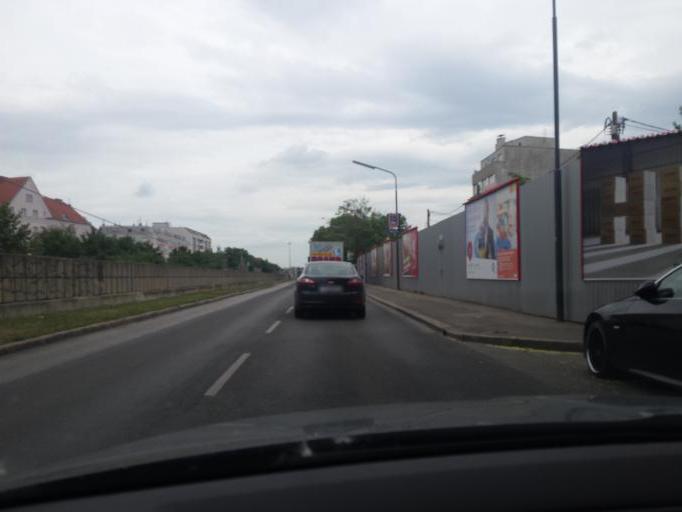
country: AT
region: Vienna
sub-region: Wien Stadt
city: Vienna
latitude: 48.1715
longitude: 16.4085
